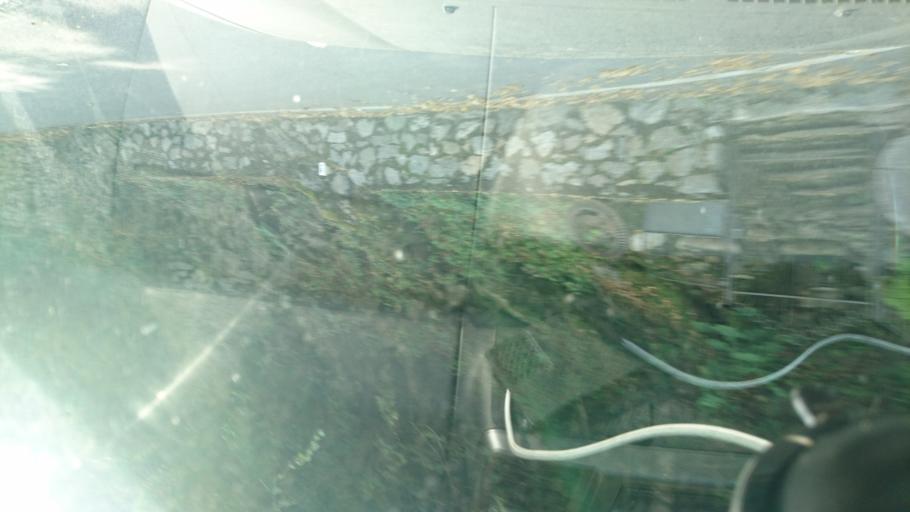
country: IT
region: Lombardy
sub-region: Provincia di Brescia
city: Paisco Loveno
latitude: 46.0771
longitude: 10.2813
